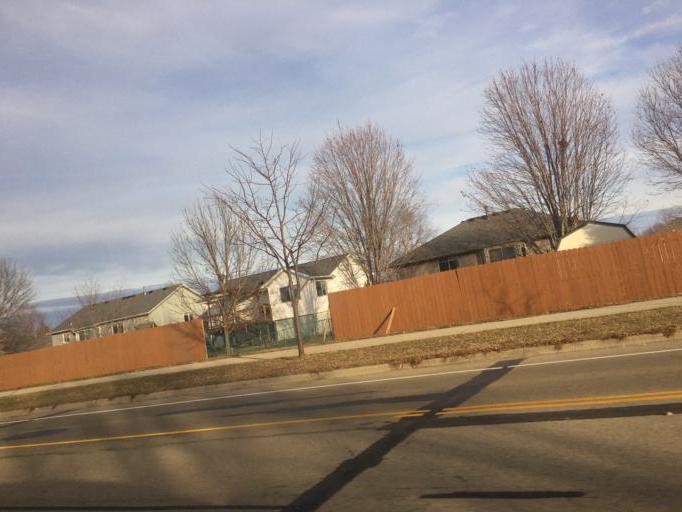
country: US
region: Minnesota
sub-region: Olmsted County
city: Oronoco
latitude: 44.0837
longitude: -92.5389
